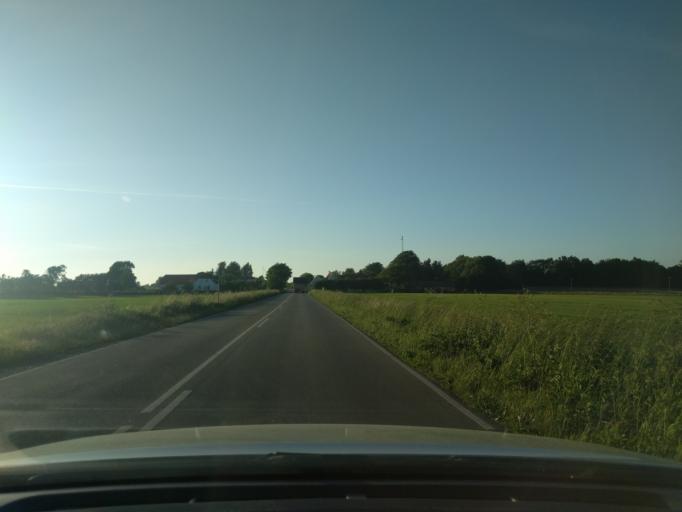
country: DK
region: South Denmark
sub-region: Kerteminde Kommune
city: Kerteminde
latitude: 55.5383
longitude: 10.6633
